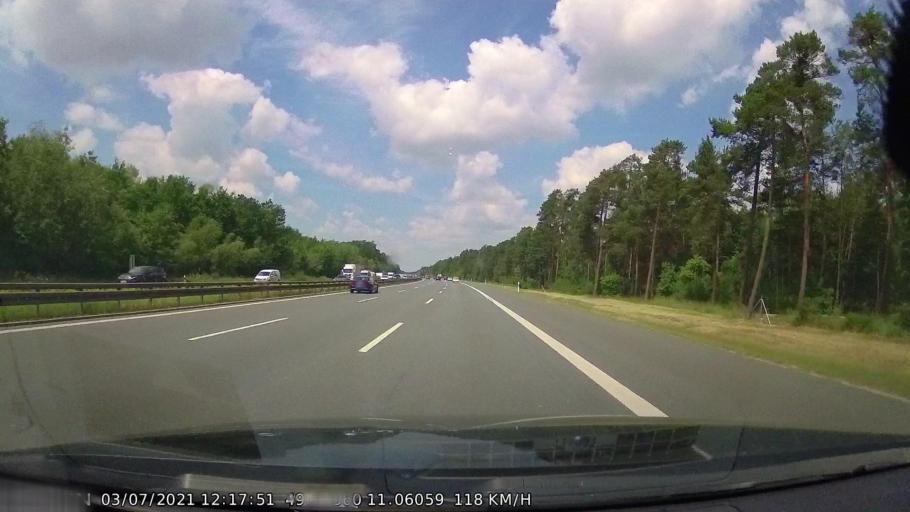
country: DE
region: Bavaria
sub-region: Regierungsbezirk Mittelfranken
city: Wetzendorf
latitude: 49.5297
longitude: 11.0603
